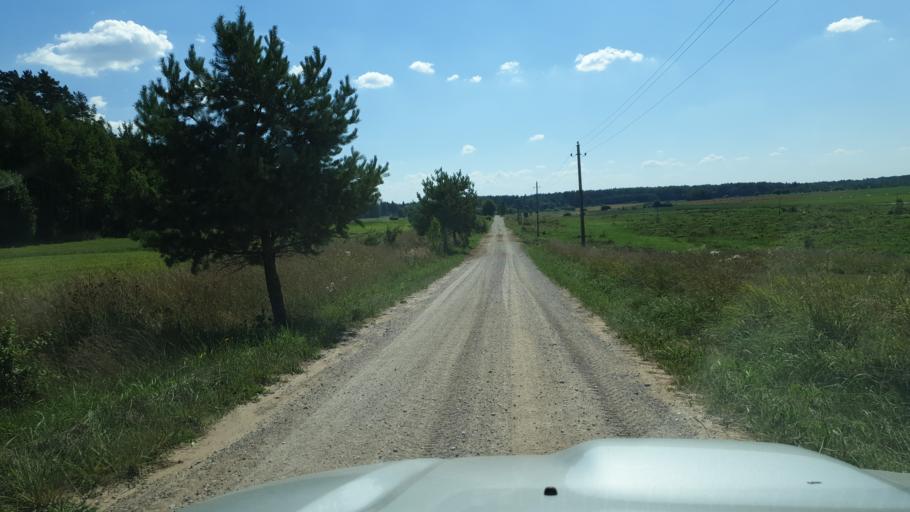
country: LT
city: Sirvintos
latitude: 54.9106
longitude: 24.9118
